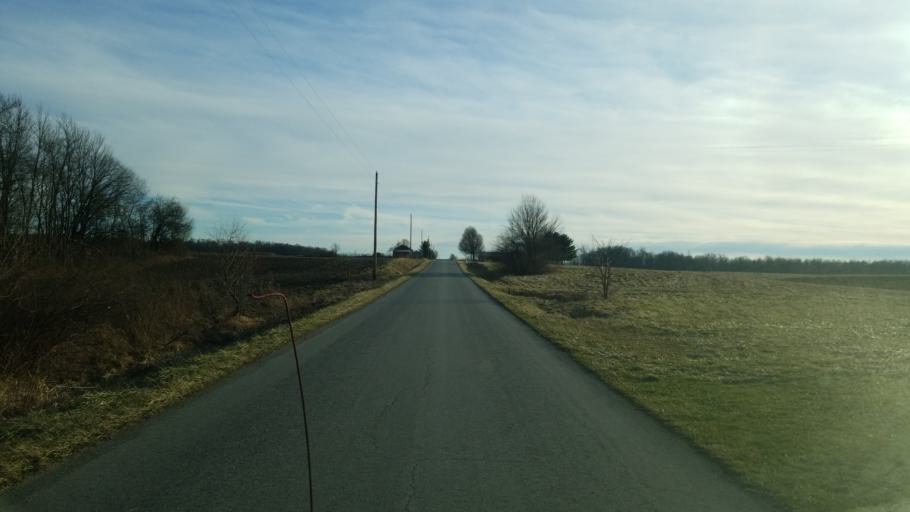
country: US
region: Ohio
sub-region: Huron County
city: Greenwich
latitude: 41.0093
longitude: -82.5348
